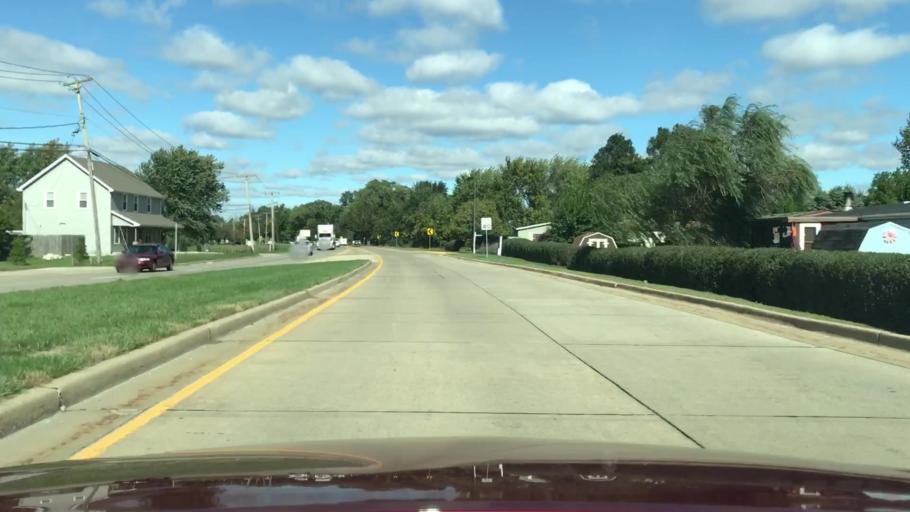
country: US
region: Illinois
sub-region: Cook County
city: Lynwood
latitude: 41.5087
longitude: -87.5345
